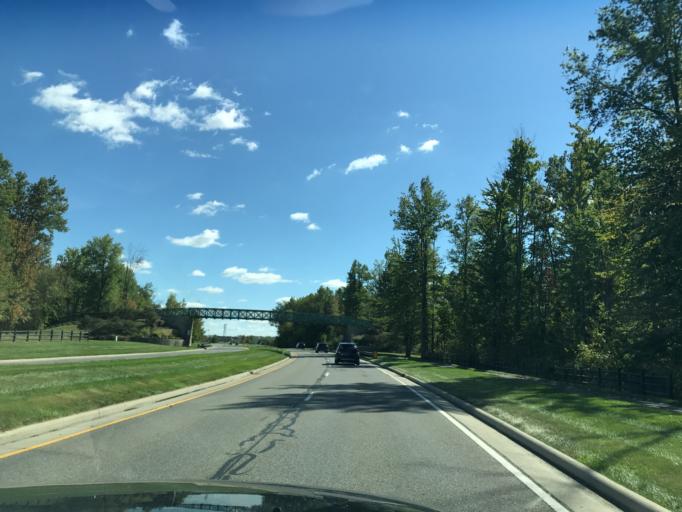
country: US
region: Ohio
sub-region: Delaware County
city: Powell
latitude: 40.1773
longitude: -83.0955
